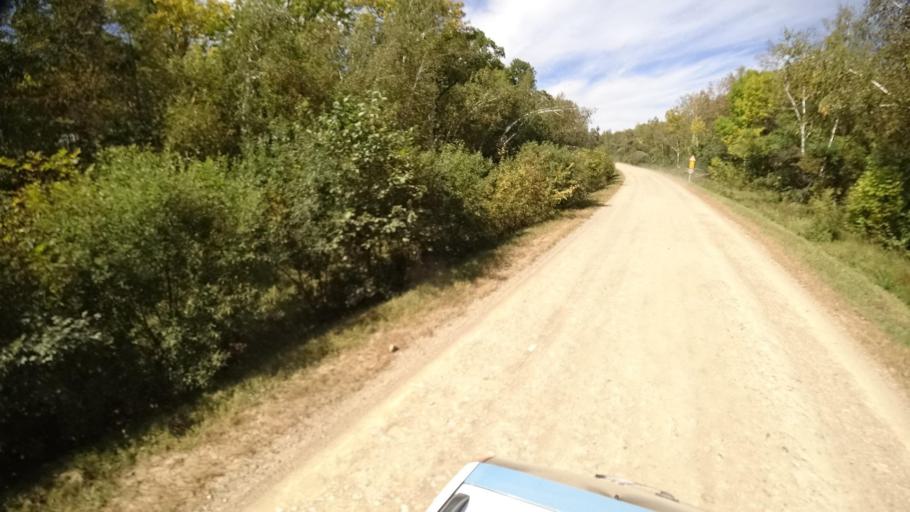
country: RU
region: Primorskiy
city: Yakovlevka
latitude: 44.6622
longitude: 133.7252
